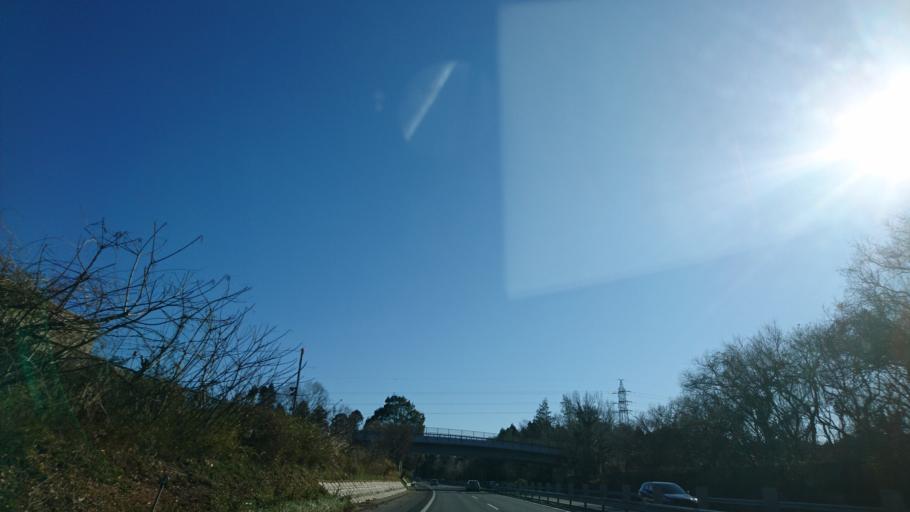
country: JP
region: Chiba
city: Chiba
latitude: 35.5751
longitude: 140.1989
